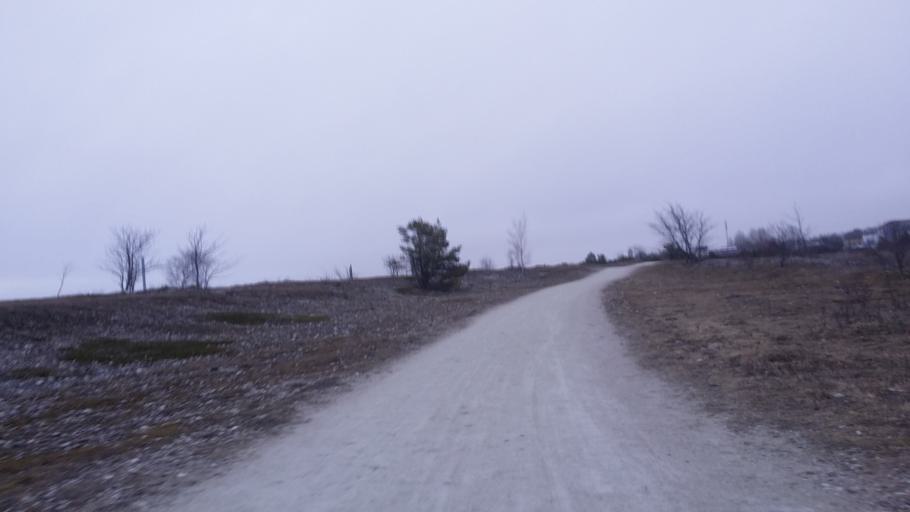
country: SE
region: Gotland
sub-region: Gotland
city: Vibble
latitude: 57.6219
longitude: 18.2688
